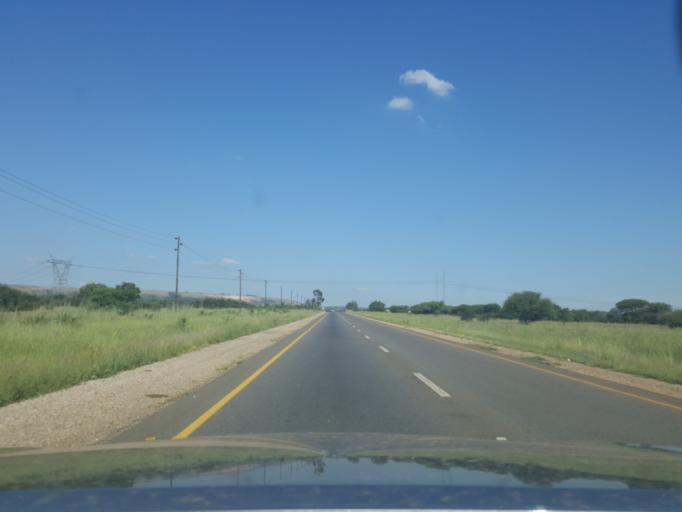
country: ZA
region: Gauteng
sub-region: City of Tshwane Metropolitan Municipality
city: Cullinan
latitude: -25.7579
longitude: 28.4069
